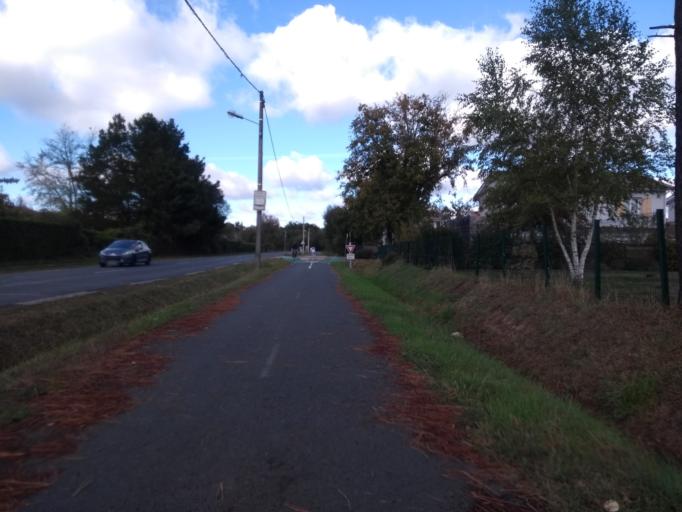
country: FR
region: Aquitaine
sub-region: Departement de la Gironde
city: Saint-Aubin-de-Medoc
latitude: 44.7961
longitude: -0.7053
